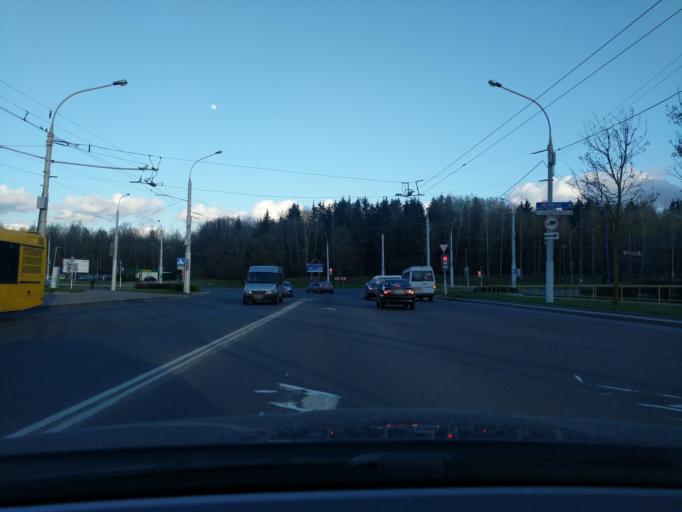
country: BY
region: Minsk
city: Novoye Medvezhino
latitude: 53.8909
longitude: 27.4546
